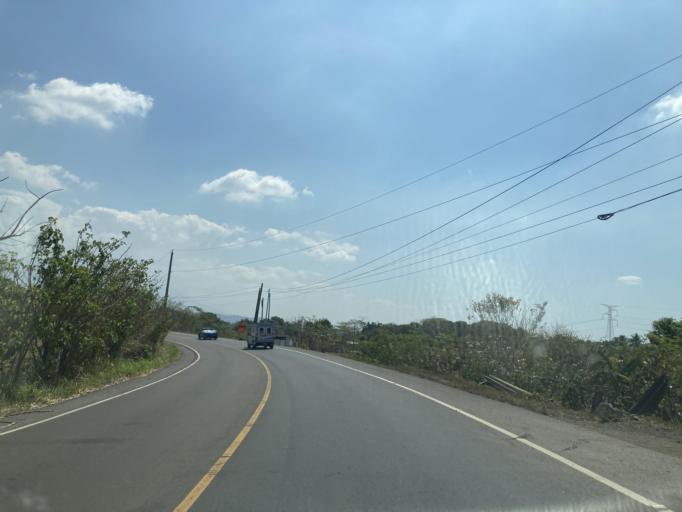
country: GT
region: Escuintla
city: Guanagazapa
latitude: 14.2011
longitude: -90.7120
